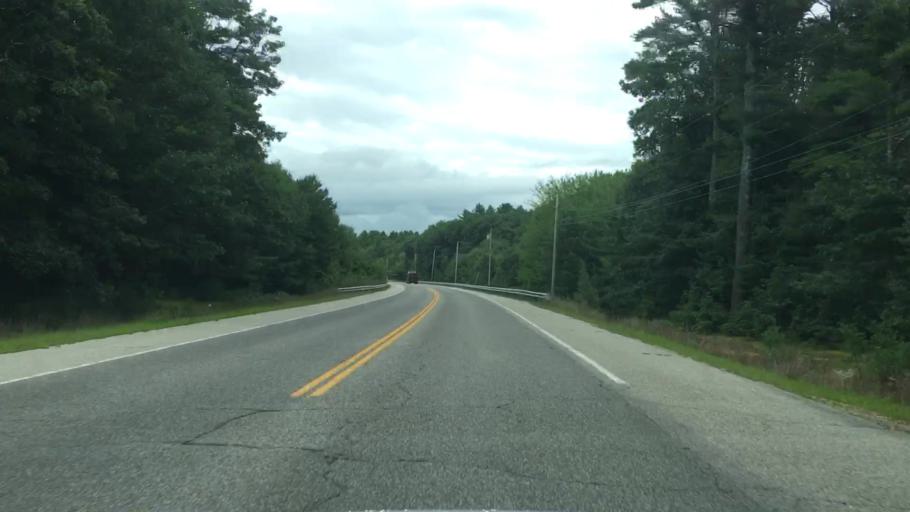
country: US
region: Maine
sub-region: York County
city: North Berwick
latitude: 43.3539
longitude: -70.7280
